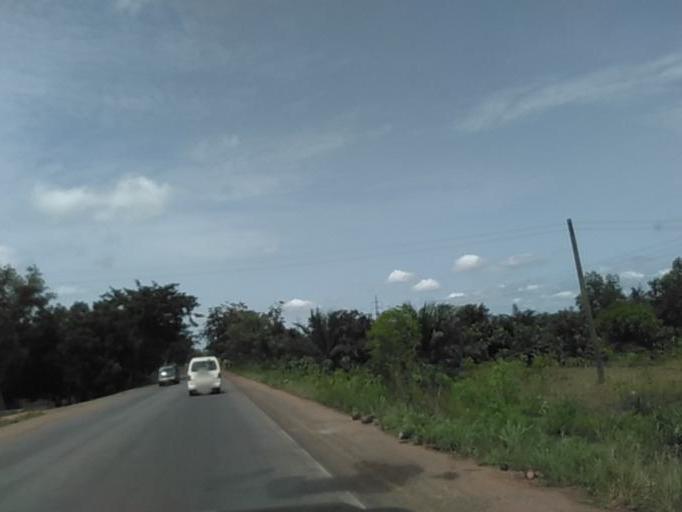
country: GH
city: Akropong
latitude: 6.1419
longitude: 0.0540
